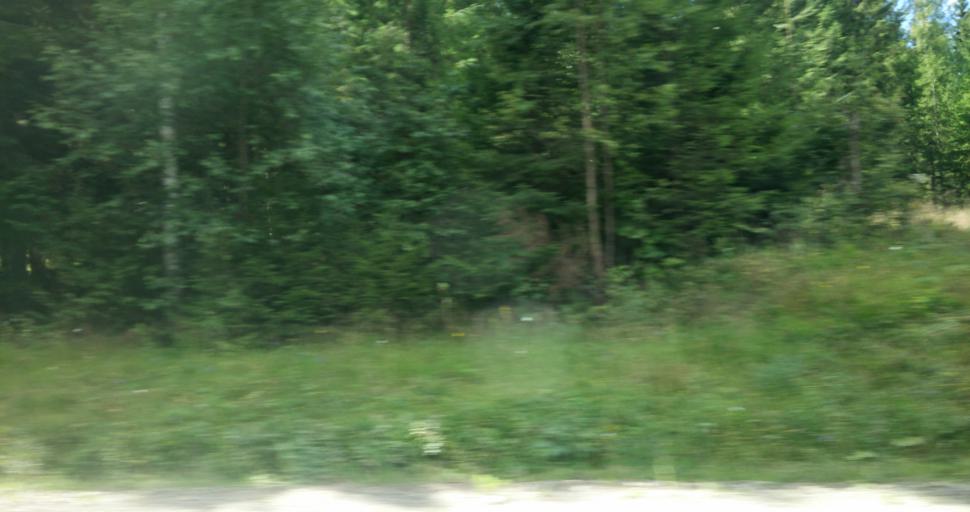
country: SE
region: Vaermland
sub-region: Hagfors Kommun
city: Ekshaerad
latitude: 60.0775
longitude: 13.4624
